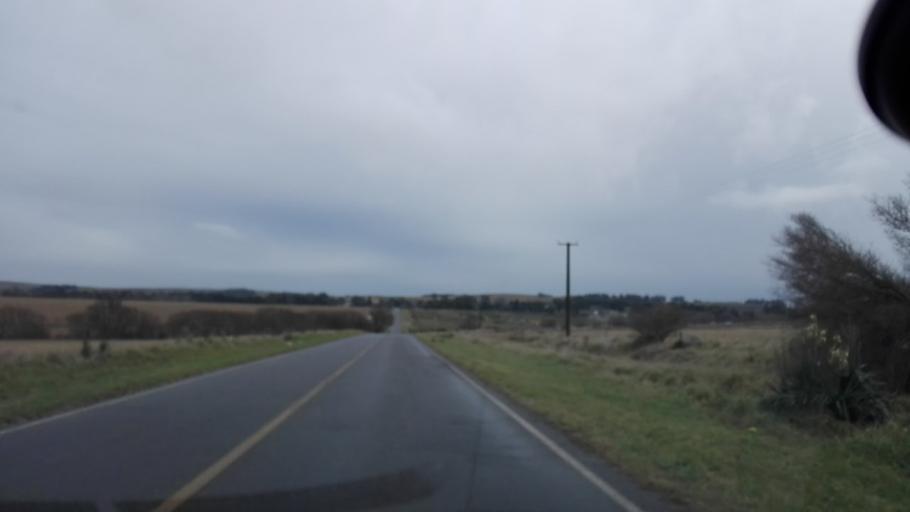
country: AR
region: Buenos Aires
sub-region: Partido de Tandil
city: Tandil
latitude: -37.3579
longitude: -59.1860
